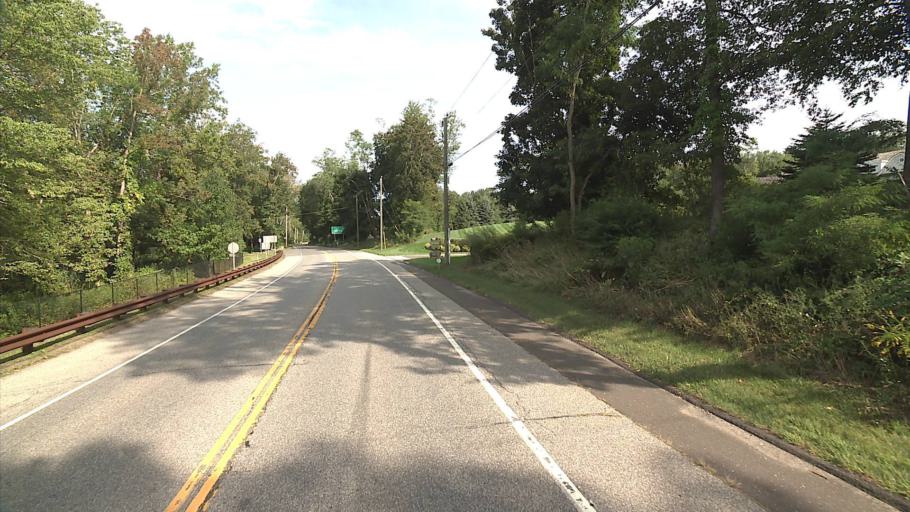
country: US
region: Connecticut
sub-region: Fairfield County
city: New Canaan
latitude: 41.2001
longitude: -73.5088
